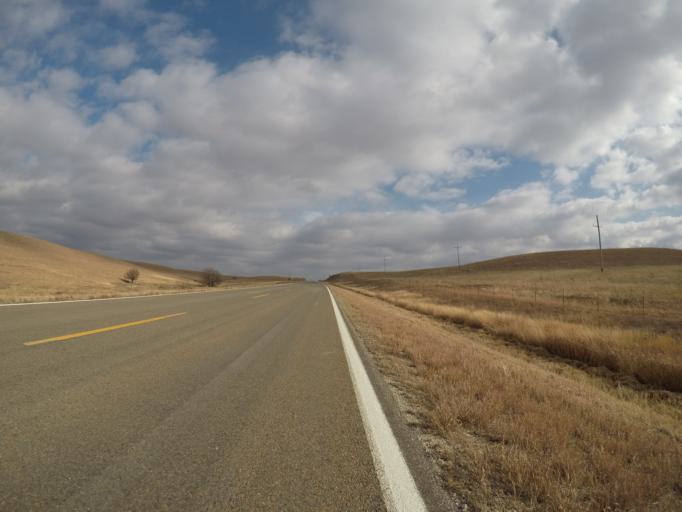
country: US
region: Kansas
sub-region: Wabaunsee County
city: Alma
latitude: 38.8701
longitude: -96.3434
